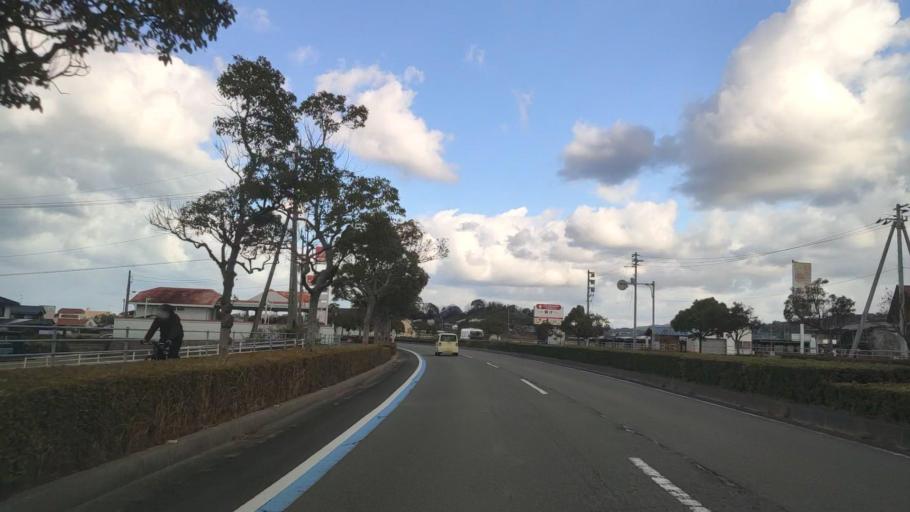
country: JP
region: Ehime
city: Hojo
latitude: 33.9433
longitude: 132.7756
